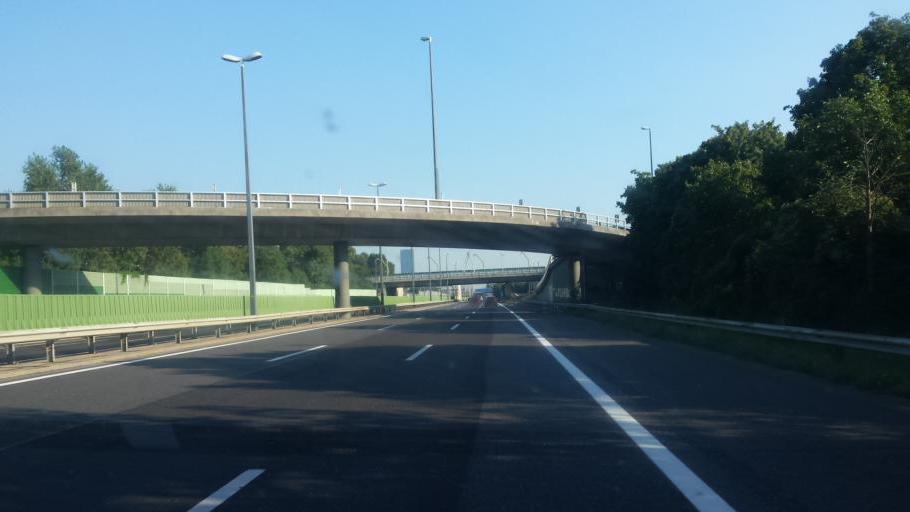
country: AT
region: Vienna
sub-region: Wien Stadt
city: Vienna
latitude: 48.2589
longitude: 16.3834
